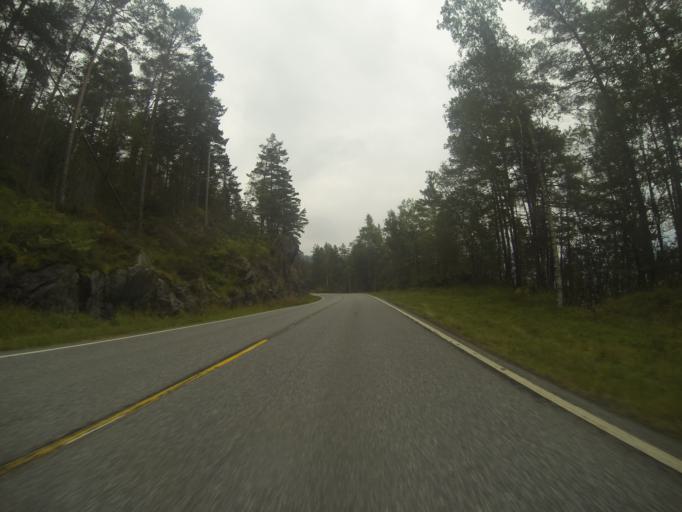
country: NO
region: Rogaland
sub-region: Suldal
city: Sand
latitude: 59.5255
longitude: 6.2463
